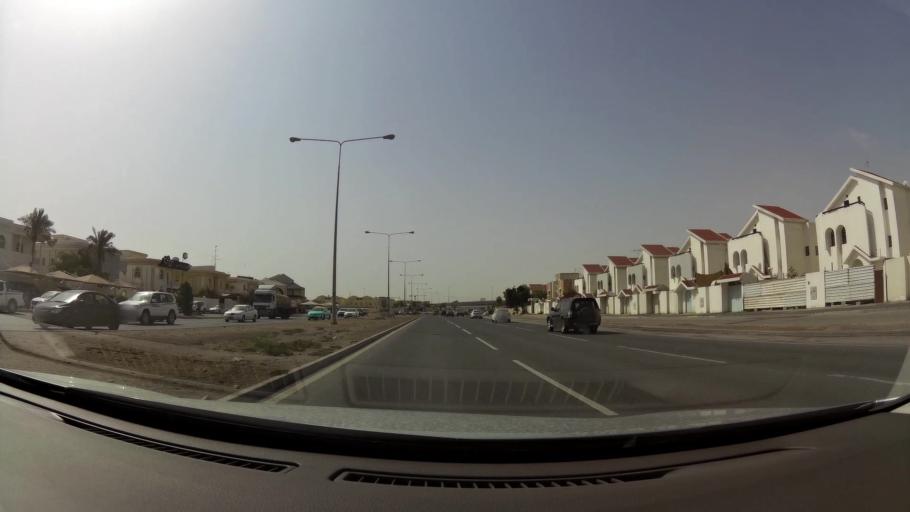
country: QA
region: Baladiyat ad Dawhah
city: Doha
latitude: 25.2432
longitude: 51.5241
